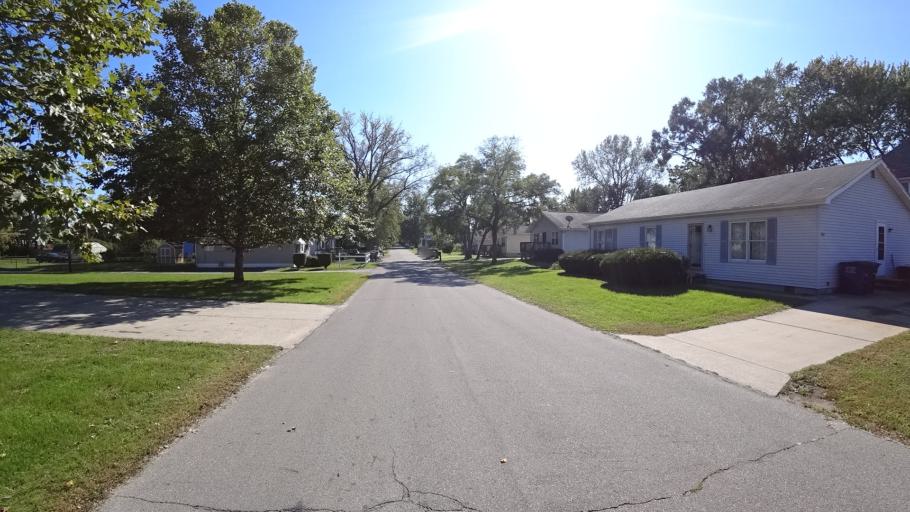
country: US
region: Indiana
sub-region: LaPorte County
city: Michigan City
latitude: 41.6947
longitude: -86.8980
